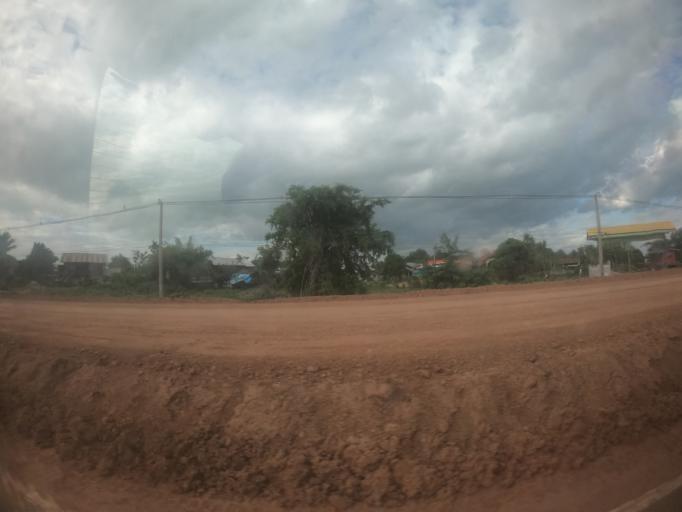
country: TH
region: Surin
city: Kap Choeng
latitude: 14.5065
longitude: 103.5570
